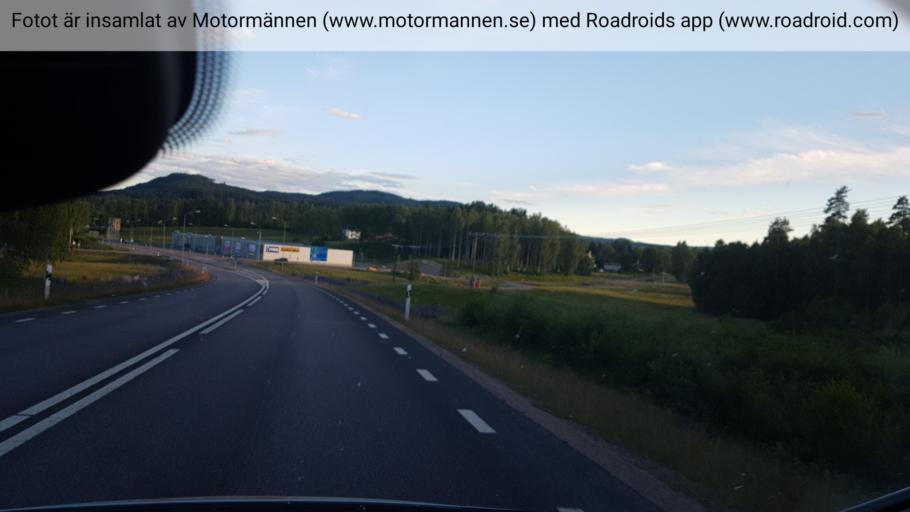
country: SE
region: Vaermland
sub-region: Torsby Kommun
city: Torsby
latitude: 60.1395
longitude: 12.9882
